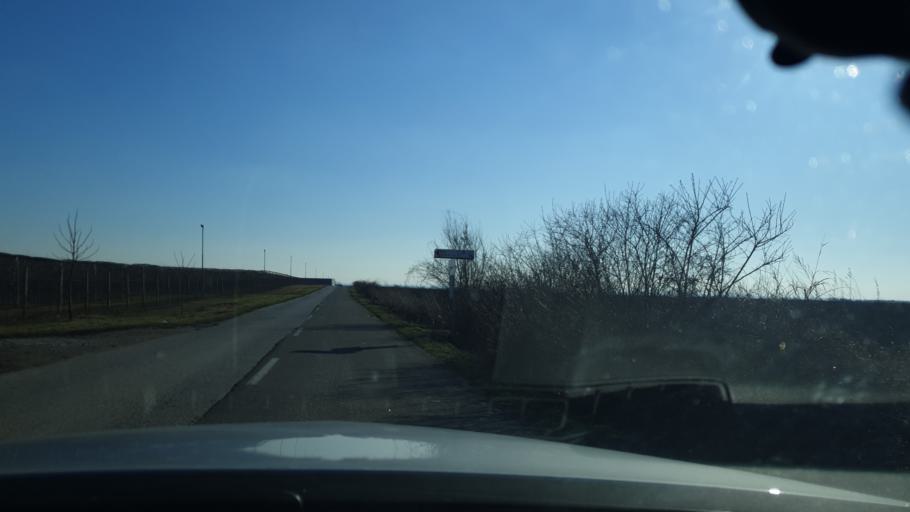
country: RS
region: Autonomna Pokrajina Vojvodina
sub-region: Sremski Okrug
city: Ruma
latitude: 45.0590
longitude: 19.8079
